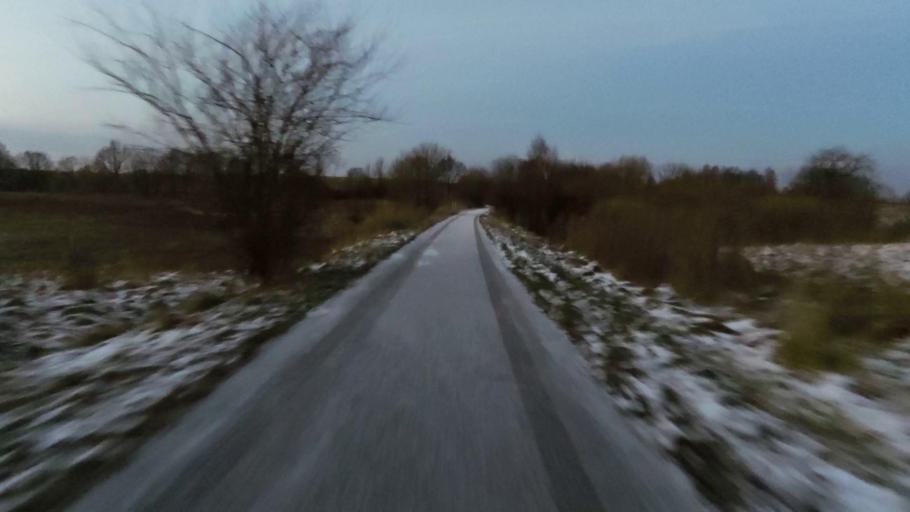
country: PL
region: West Pomeranian Voivodeship
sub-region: Powiat swidwinski
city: Polczyn-Zdroj
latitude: 53.7678
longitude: 16.0696
